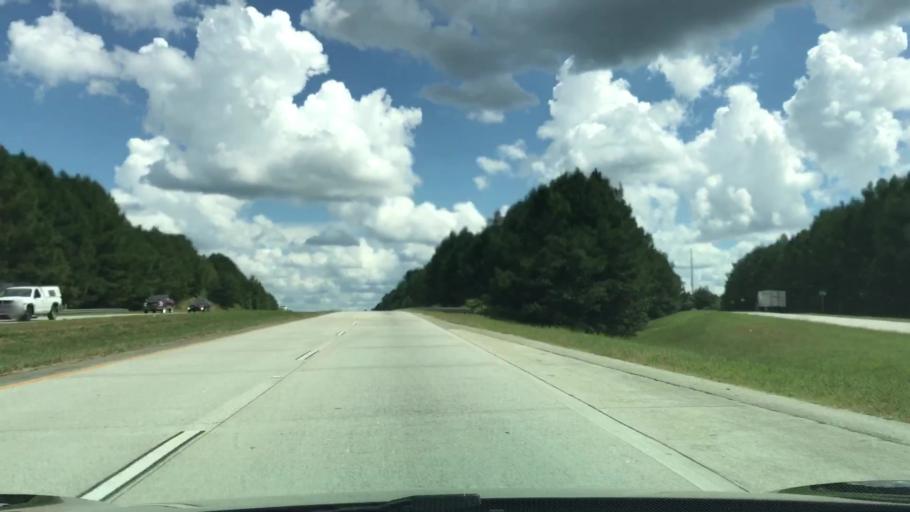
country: US
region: Georgia
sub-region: Oconee County
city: Bogart
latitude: 33.9261
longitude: -83.5174
